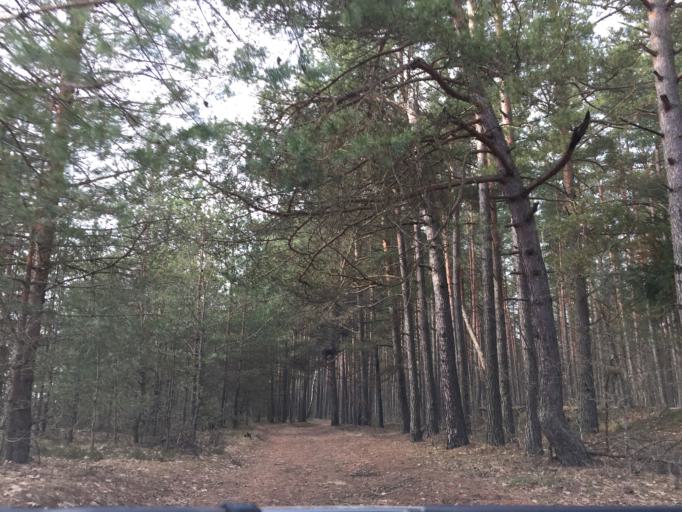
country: LV
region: Stopini
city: Ulbroka
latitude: 56.9211
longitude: 24.3064
